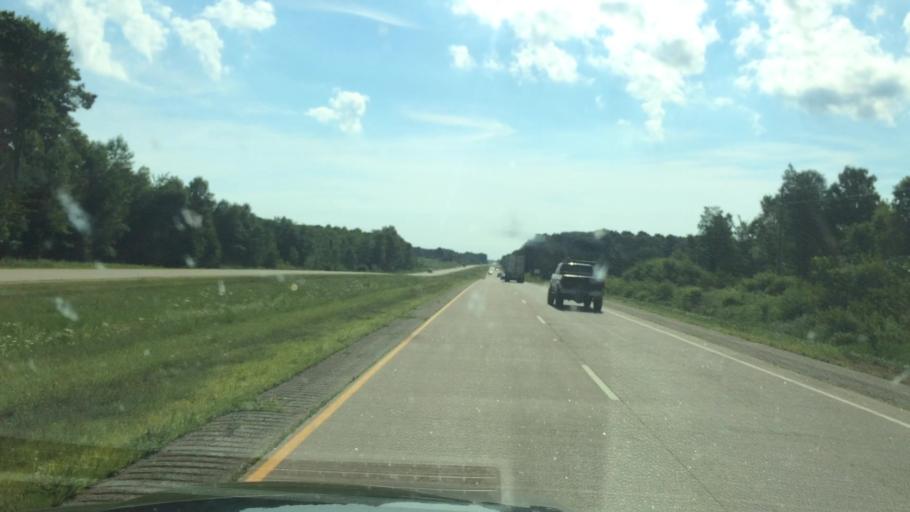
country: US
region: Wisconsin
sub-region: Waupaca County
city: Marion
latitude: 44.8040
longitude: -88.9772
